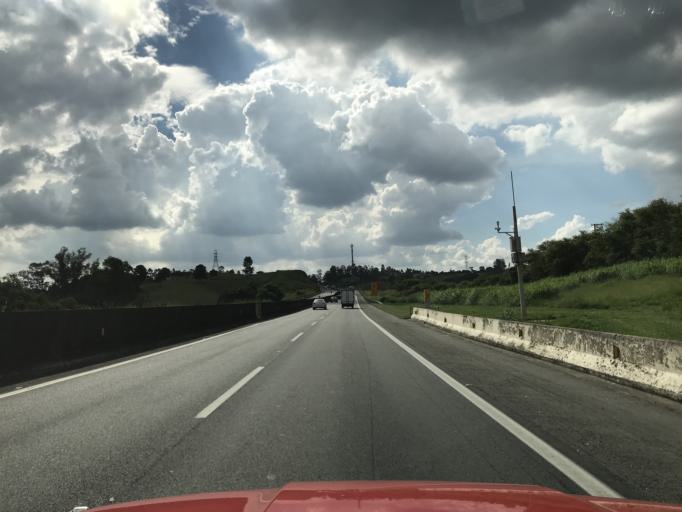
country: BR
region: Sao Paulo
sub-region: Vinhedo
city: Vinhedo
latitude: -23.0360
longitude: -47.0098
